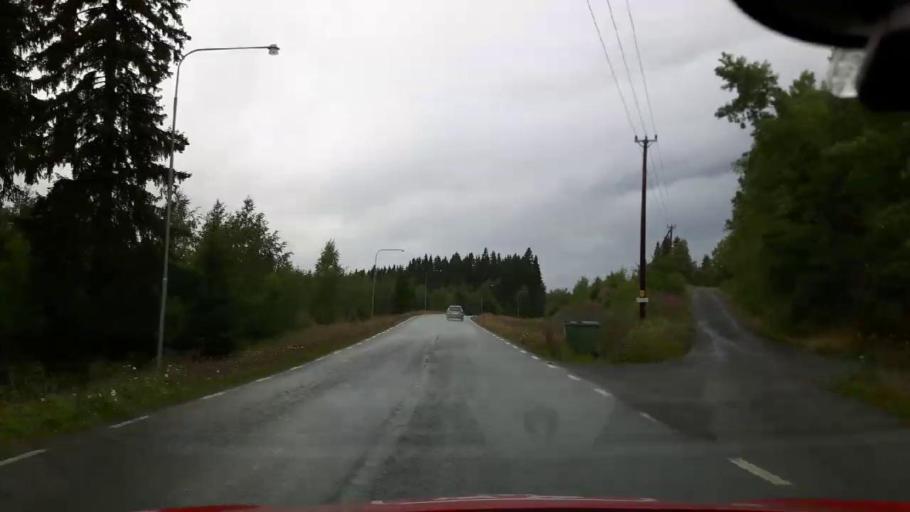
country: SE
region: Jaemtland
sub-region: Krokoms Kommun
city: Krokom
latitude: 63.3544
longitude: 14.1614
